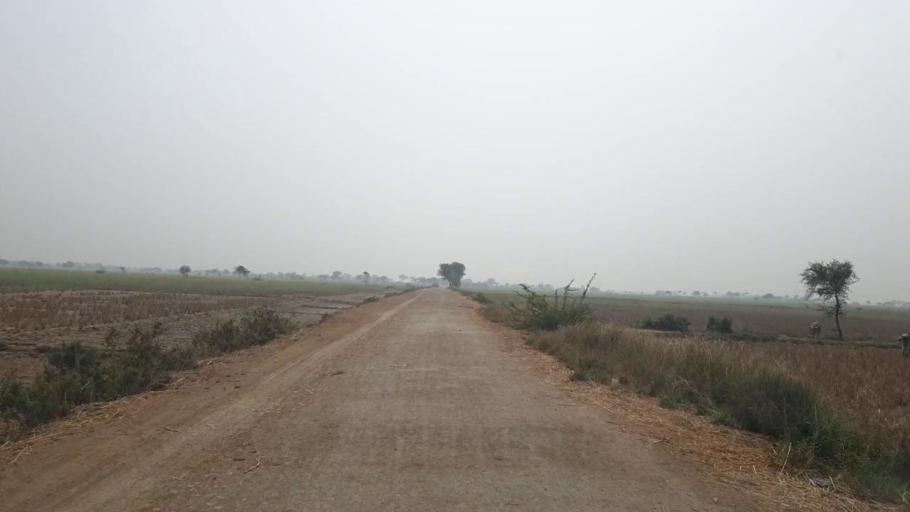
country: PK
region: Sindh
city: Kario
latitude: 24.6520
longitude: 68.6217
